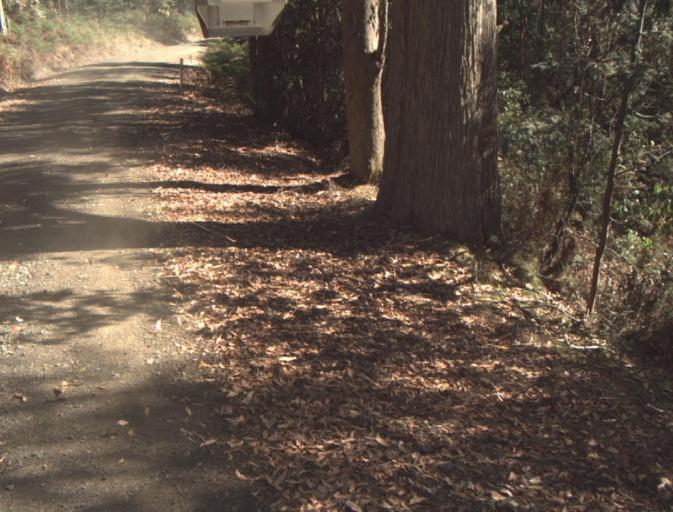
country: AU
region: Tasmania
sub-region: Dorset
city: Scottsdale
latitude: -41.2731
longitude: 147.3751
